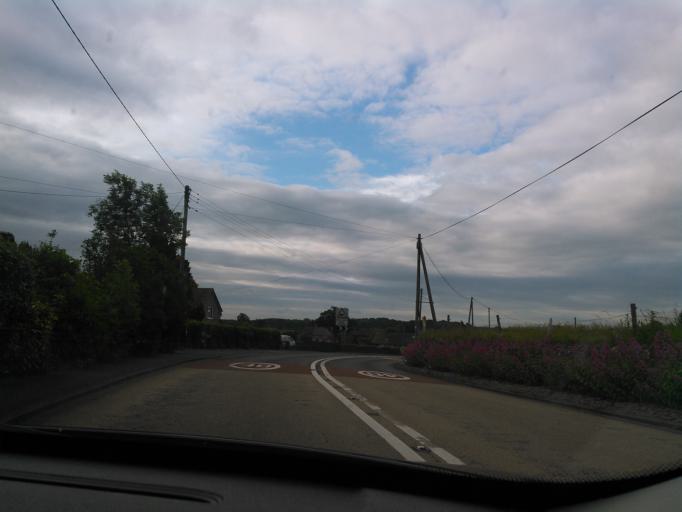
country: GB
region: England
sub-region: Shropshire
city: Clive
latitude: 52.8191
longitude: -2.6879
